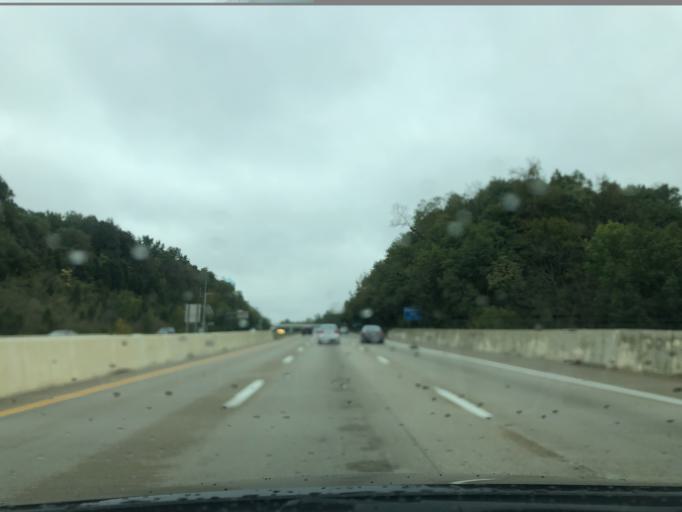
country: US
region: Ohio
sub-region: Hamilton County
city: The Village of Indian Hill
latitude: 39.2382
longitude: -84.2969
